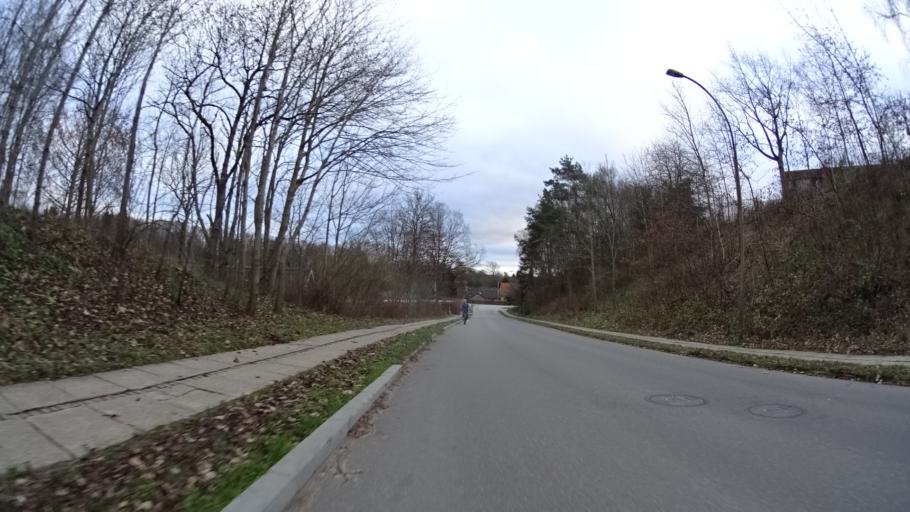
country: DK
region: Central Jutland
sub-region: Arhus Kommune
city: Stavtrup
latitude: 56.1600
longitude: 10.1186
